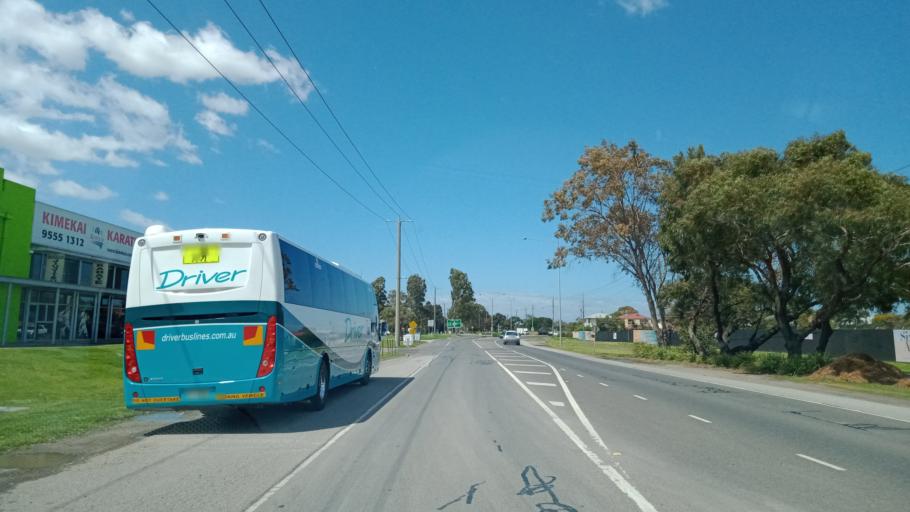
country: AU
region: Victoria
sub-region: Kingston
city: Chelsea Heights
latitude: -38.0417
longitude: 145.1387
